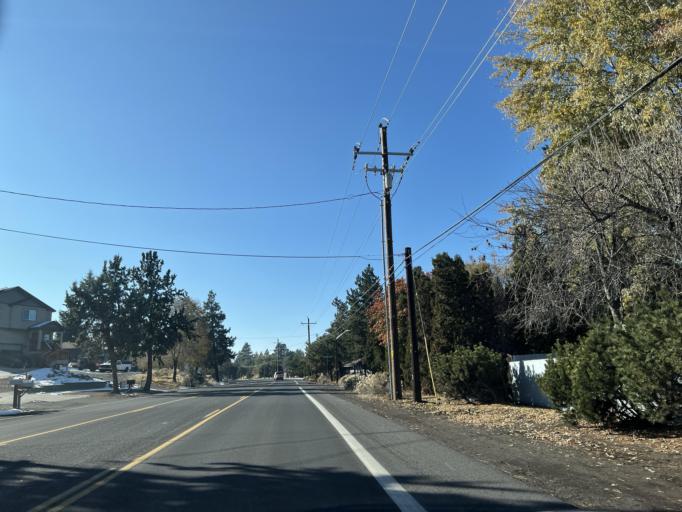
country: US
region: Oregon
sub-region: Deschutes County
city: Bend
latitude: 44.0778
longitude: -121.2860
